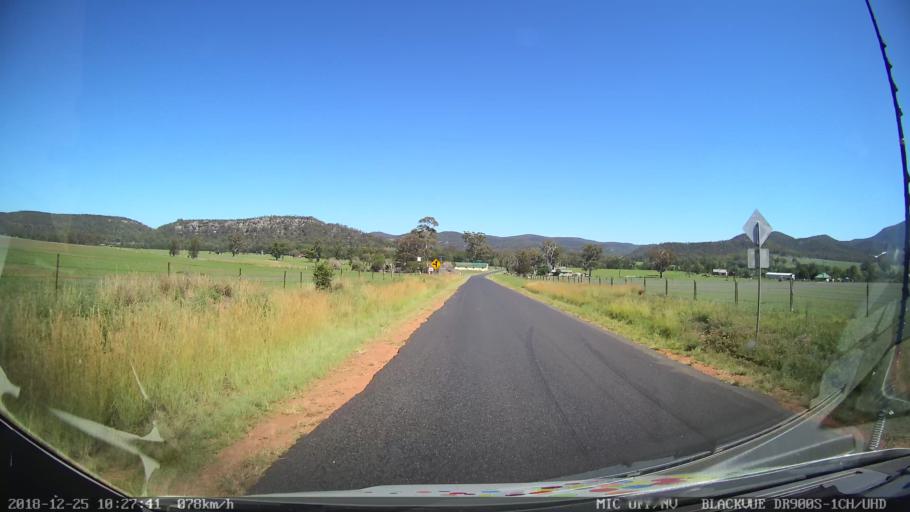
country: AU
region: New South Wales
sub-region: Muswellbrook
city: Denman
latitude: -32.3885
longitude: 150.4696
